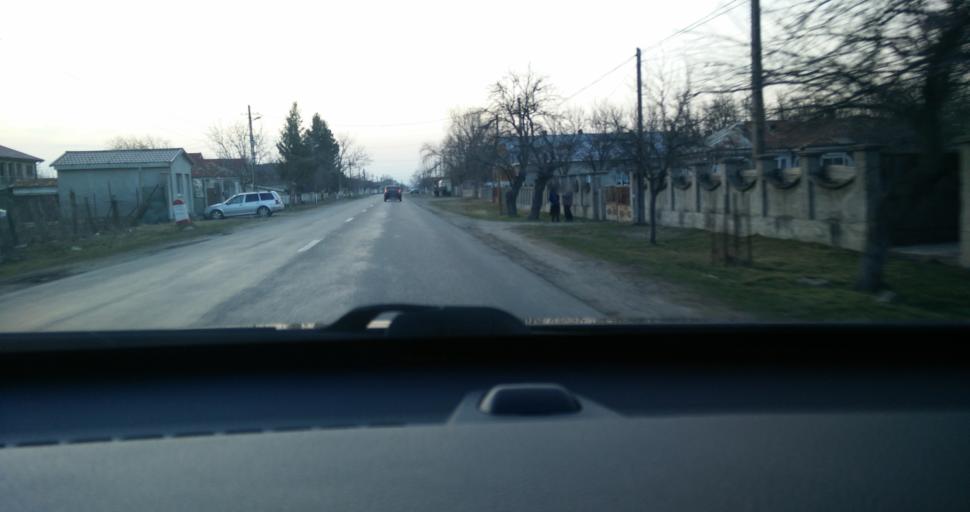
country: RO
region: Vrancea
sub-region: Comuna Rastoaca
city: Rastoaca
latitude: 45.6653
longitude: 27.2717
